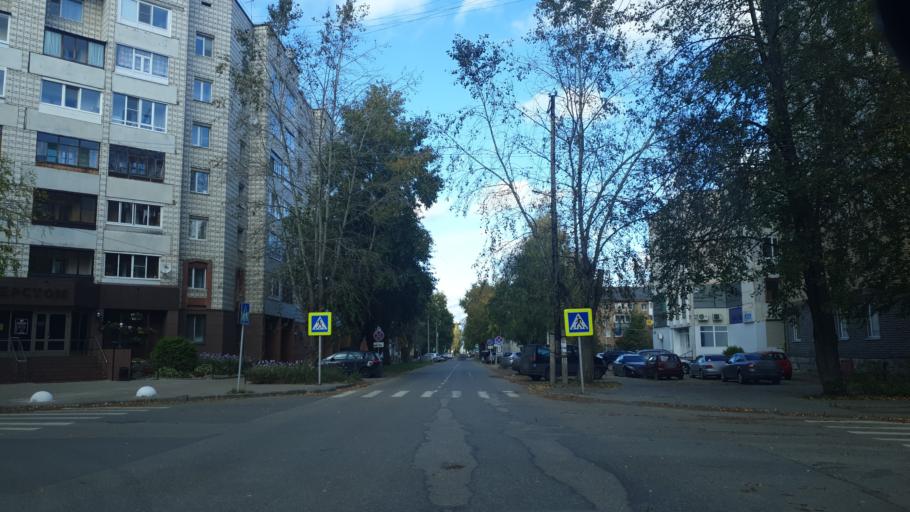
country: RU
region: Komi Republic
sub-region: Syktyvdinskiy Rayon
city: Syktyvkar
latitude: 61.6639
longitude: 50.8446
